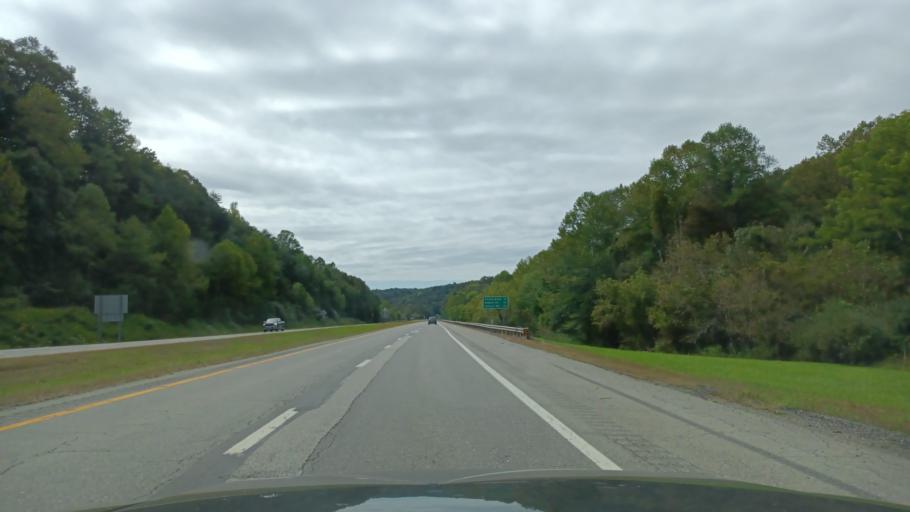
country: US
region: Ohio
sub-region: Washington County
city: Newport
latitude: 39.2405
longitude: -81.2116
